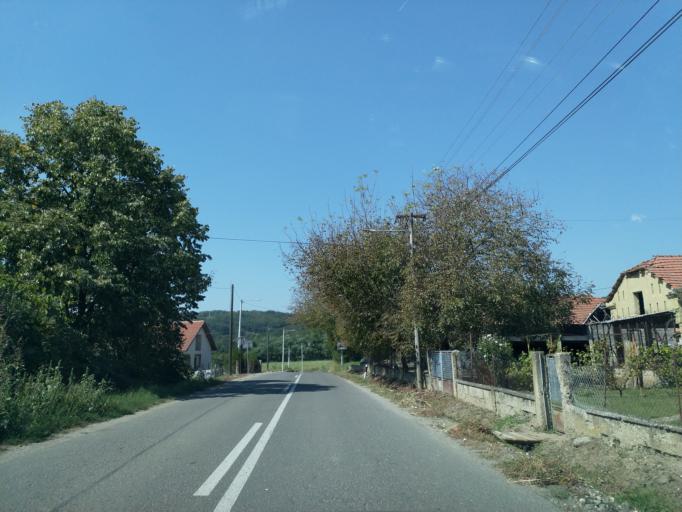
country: RS
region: Central Serbia
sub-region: Rasinski Okrug
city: Krusevac
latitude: 43.6254
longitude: 21.3409
